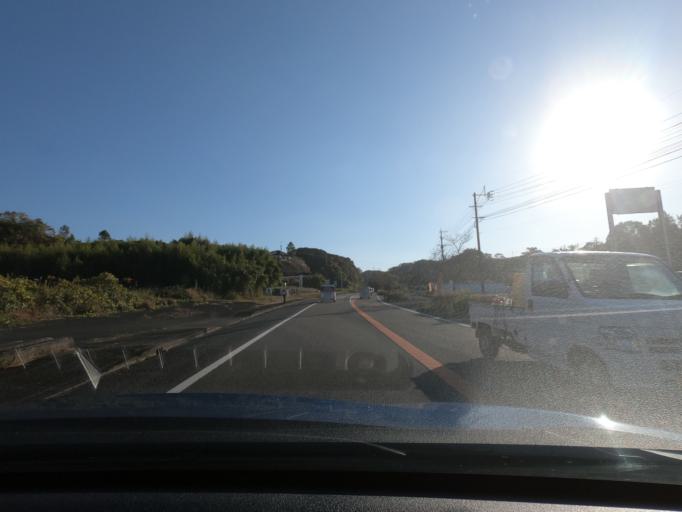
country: JP
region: Kagoshima
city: Akune
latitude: 32.0588
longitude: 130.2224
